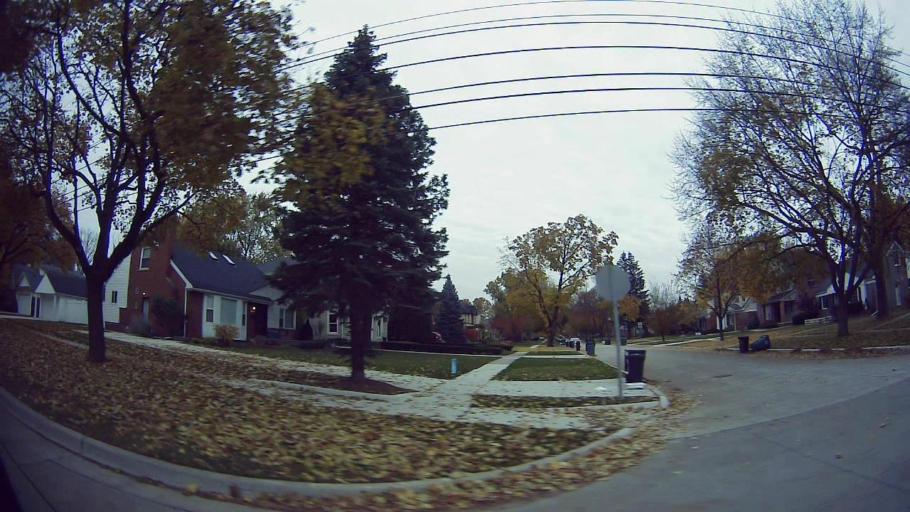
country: US
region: Michigan
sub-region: Oakland County
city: Beverly Hills
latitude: 42.5315
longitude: -83.2204
